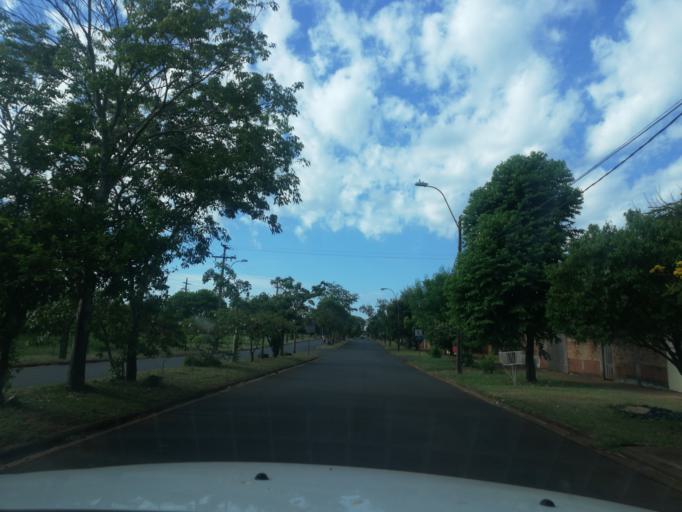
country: PY
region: Itapua
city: Encarnacion
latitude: -27.3487
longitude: -55.8489
